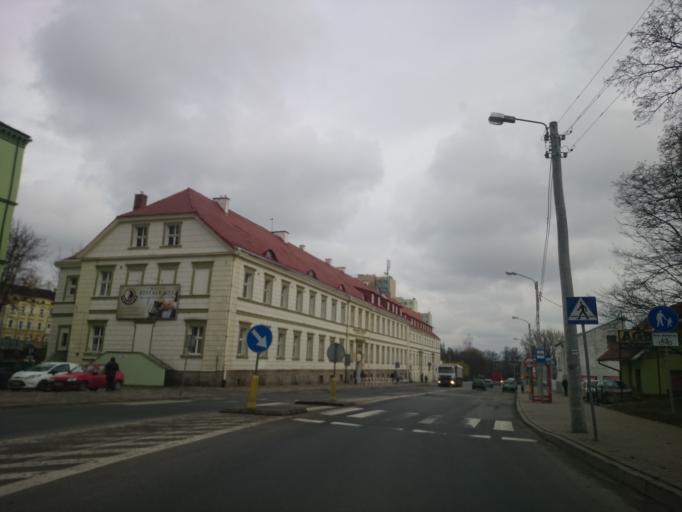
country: PL
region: Opole Voivodeship
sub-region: Powiat nyski
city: Nysa
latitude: 50.4792
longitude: 17.3197
